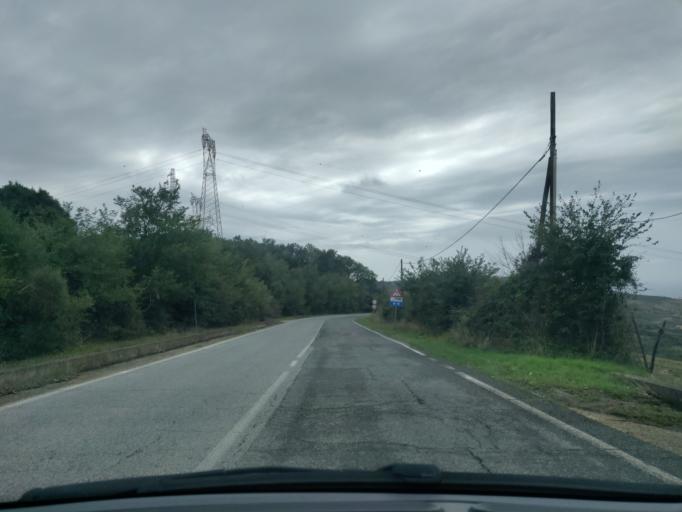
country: IT
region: Latium
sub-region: Citta metropolitana di Roma Capitale
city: Allumiere
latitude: 42.1248
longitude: 11.8641
